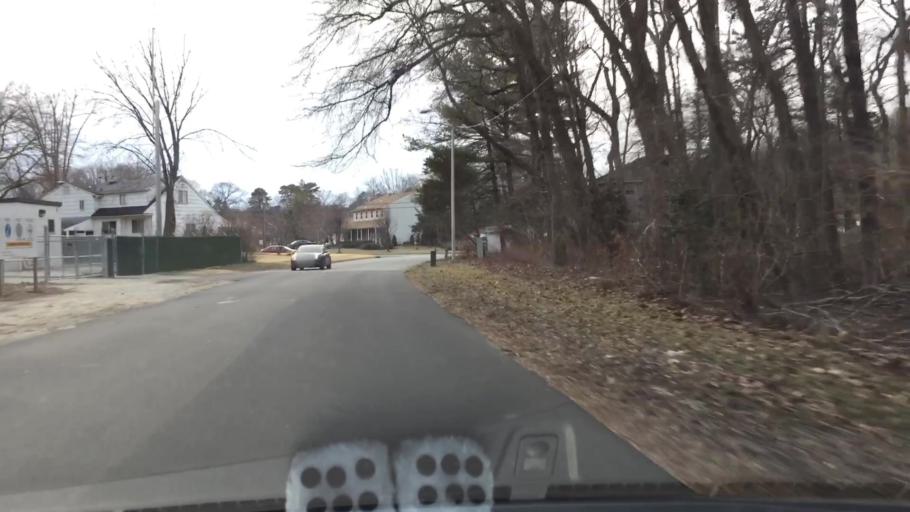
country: US
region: New Jersey
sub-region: Gloucester County
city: Turnersville
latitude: 39.7601
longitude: -75.0568
